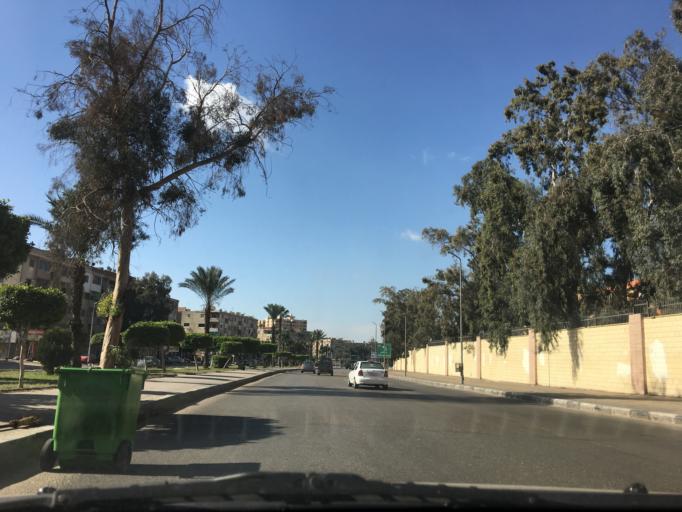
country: EG
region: Muhafazat al Qahirah
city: Cairo
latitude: 30.0504
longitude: 31.3183
